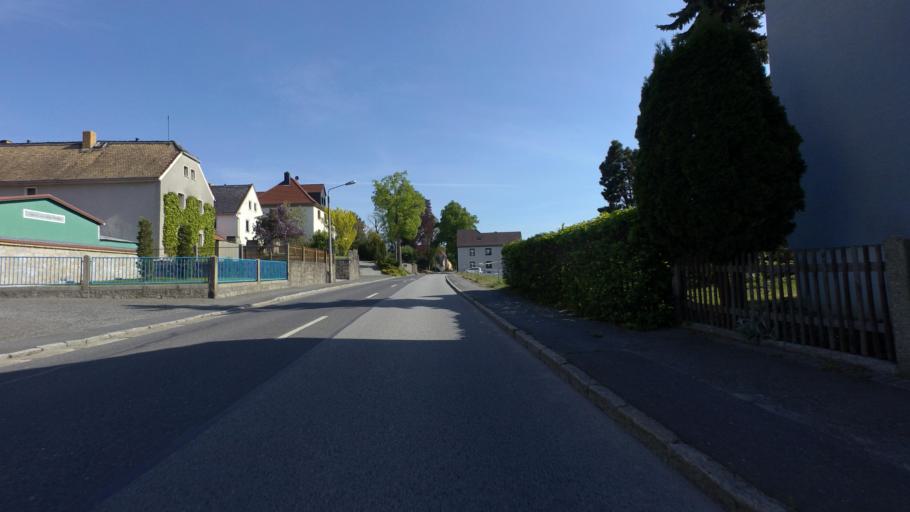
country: DE
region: Saxony
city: Kamenz
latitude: 51.2554
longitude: 14.1190
